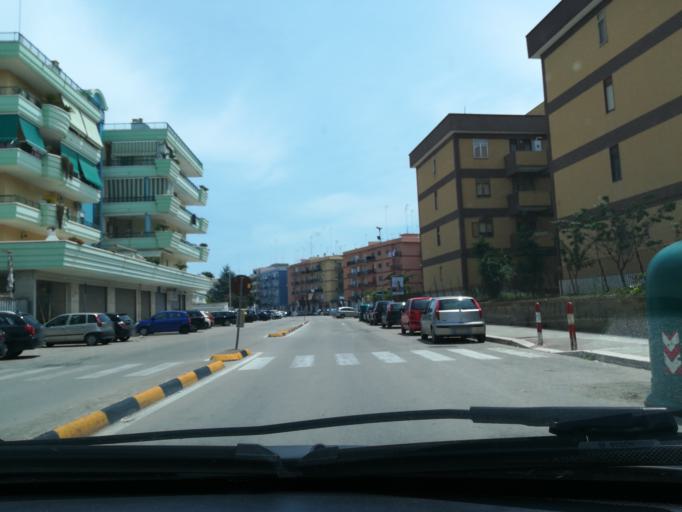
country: IT
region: Apulia
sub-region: Provincia di Barletta - Andria - Trani
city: Barletta
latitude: 41.3230
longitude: 16.2682
